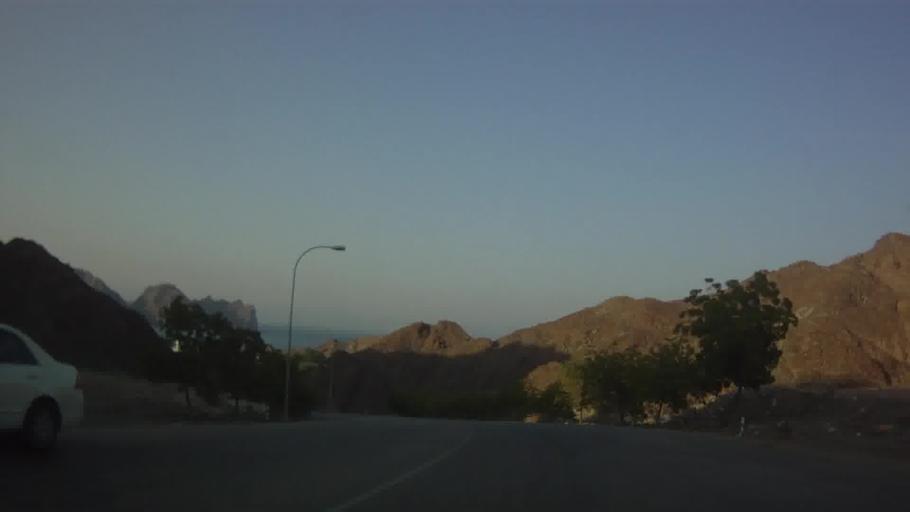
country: OM
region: Muhafazat Masqat
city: Muscat
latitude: 23.5895
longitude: 58.6026
